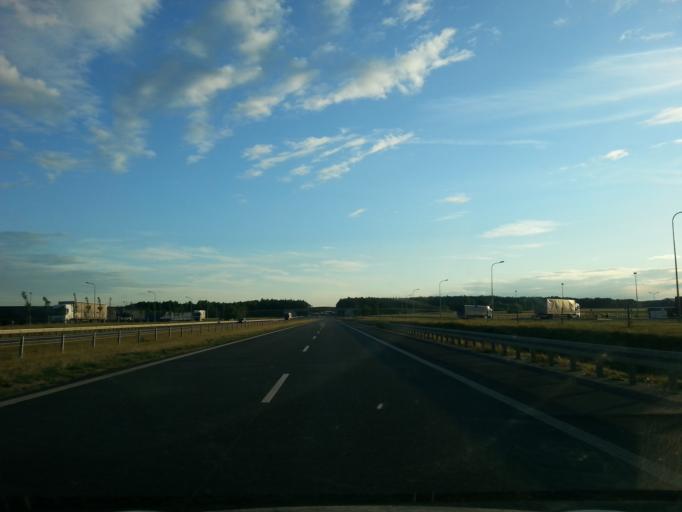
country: PL
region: Lodz Voivodeship
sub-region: Powiat wieruszowski
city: Galewice
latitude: 51.3113
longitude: 18.2424
